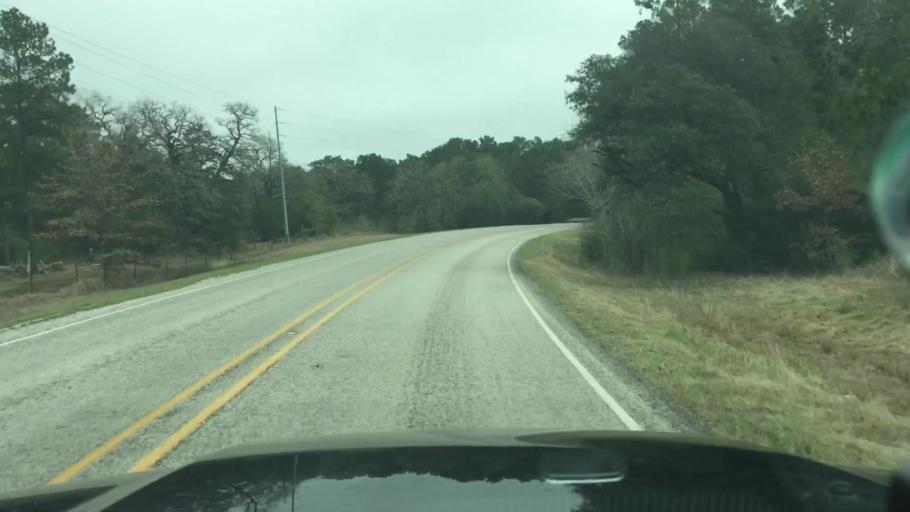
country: US
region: Texas
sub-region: Fayette County
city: La Grange
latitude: 30.0126
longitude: -96.9250
